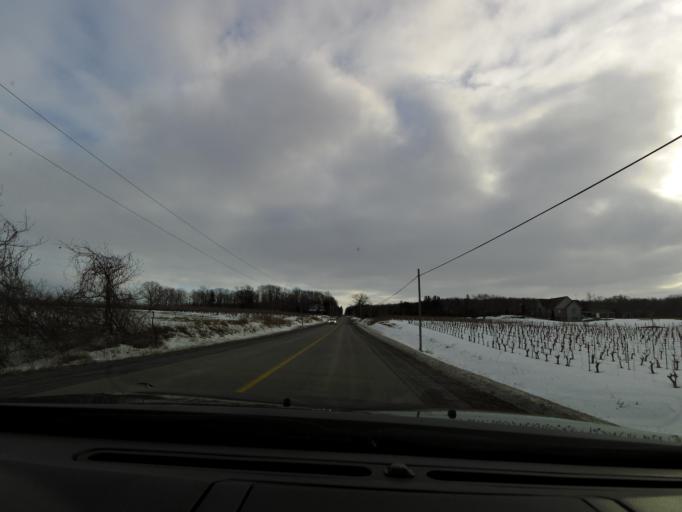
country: CA
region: Ontario
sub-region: Regional Municipality of Niagara
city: St. Catharines
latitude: 43.1701
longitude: -79.4973
